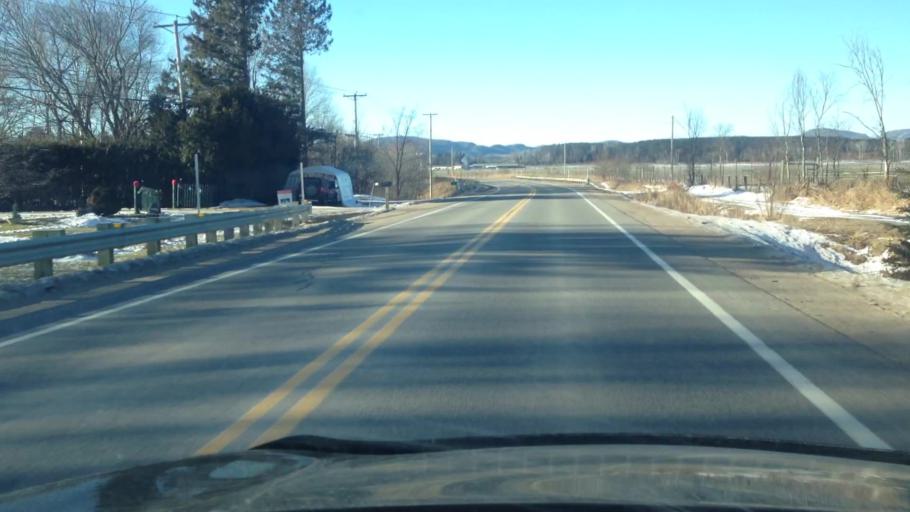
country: CA
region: Quebec
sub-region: Laurentides
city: Mont-Tremblant
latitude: 45.9618
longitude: -74.5833
